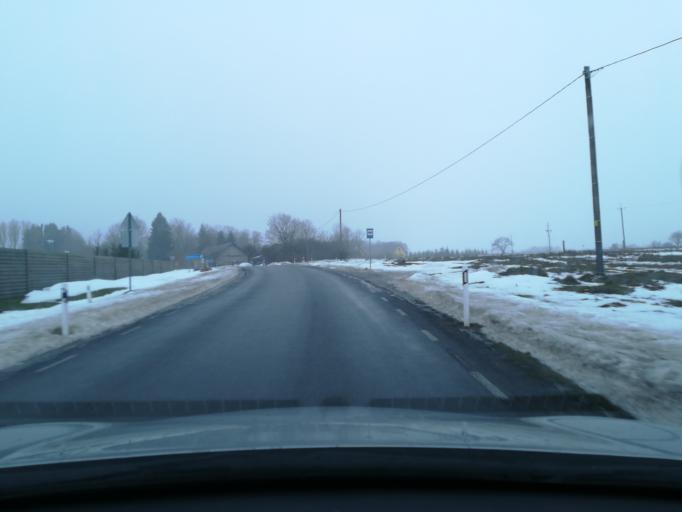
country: EE
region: Harju
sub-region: Rae vald
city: Jueri
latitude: 59.3797
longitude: 24.8879
